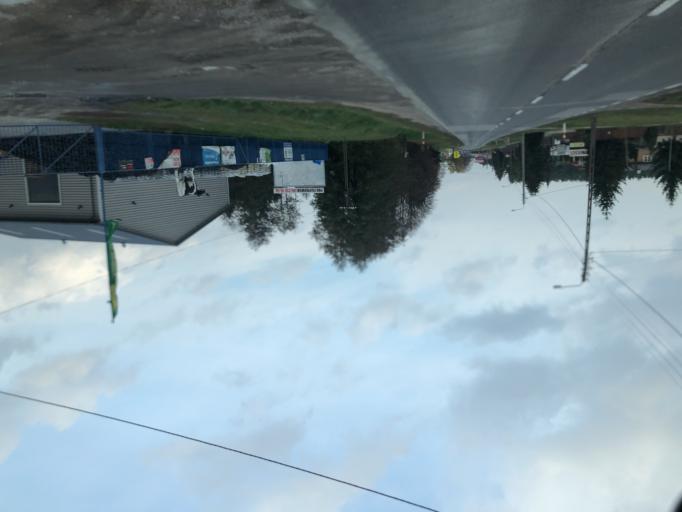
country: PL
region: Podlasie
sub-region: Lomza
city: Lomza
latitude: 53.1421
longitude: 22.0447
